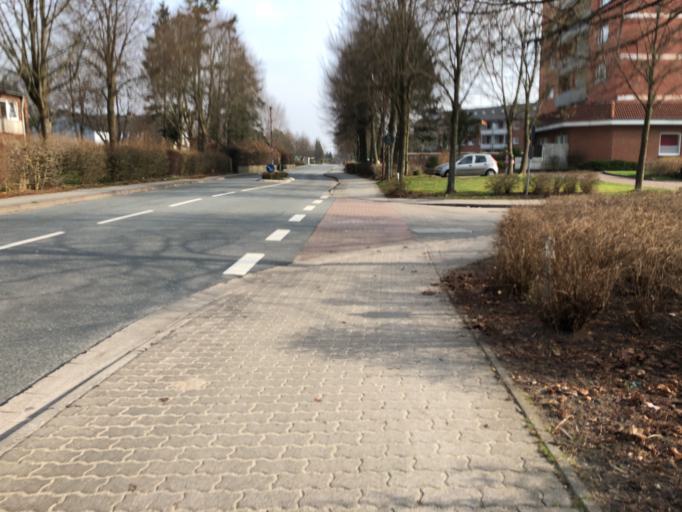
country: DE
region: Schleswig-Holstein
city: Tarp
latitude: 54.6656
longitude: 9.4070
